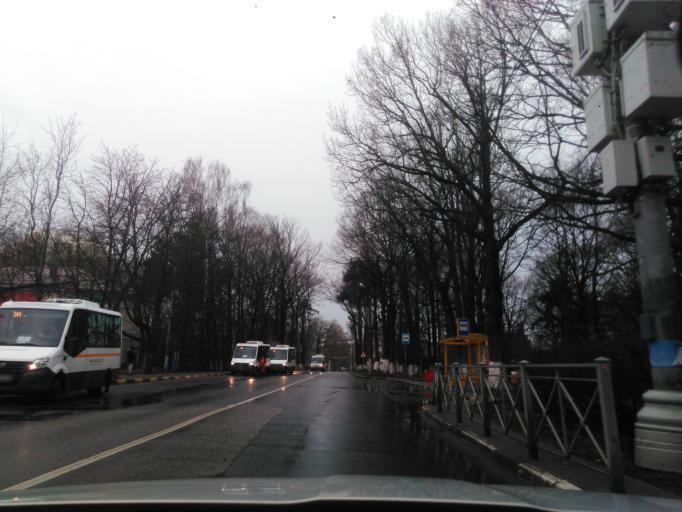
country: RU
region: Moskovskaya
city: Levoberezhnaya
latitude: 55.8927
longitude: 37.4719
